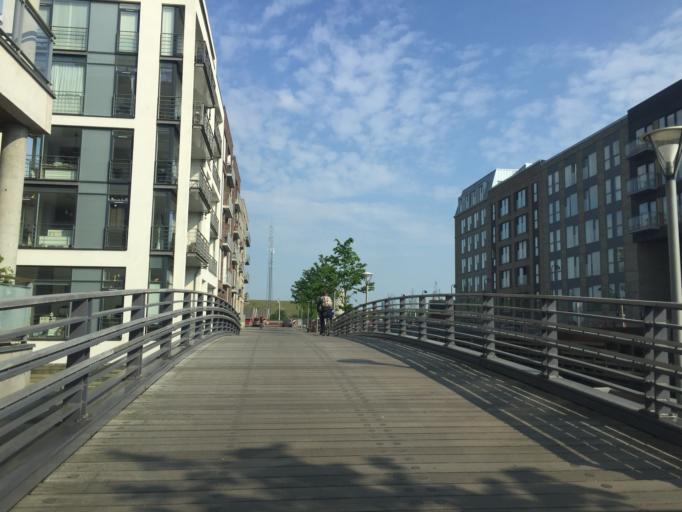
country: DK
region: Capital Region
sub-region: Kobenhavn
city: Copenhagen
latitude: 55.6451
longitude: 12.5509
